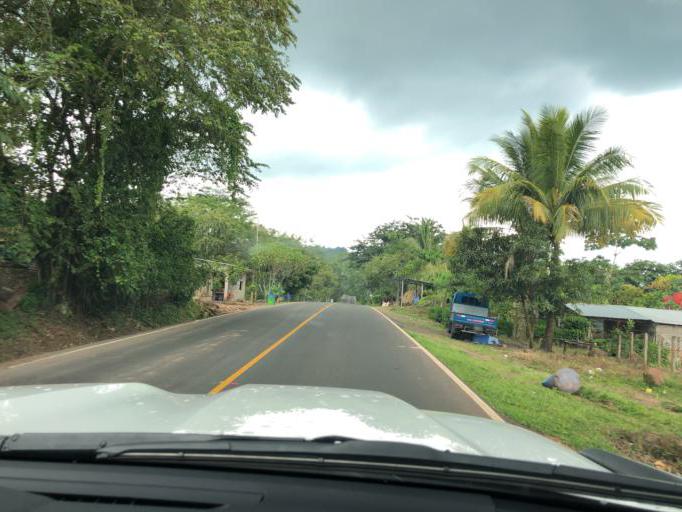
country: NI
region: Chontales
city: Villa Sandino
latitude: 11.9907
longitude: -84.8247
